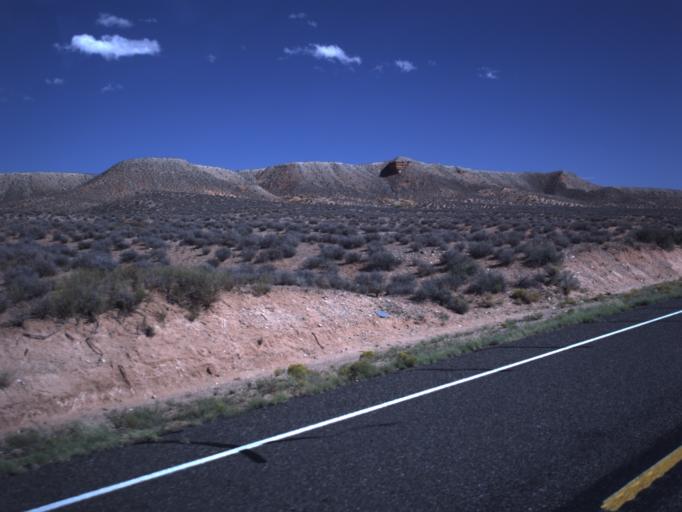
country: US
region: Utah
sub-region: Wayne County
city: Loa
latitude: 38.0908
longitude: -110.6181
